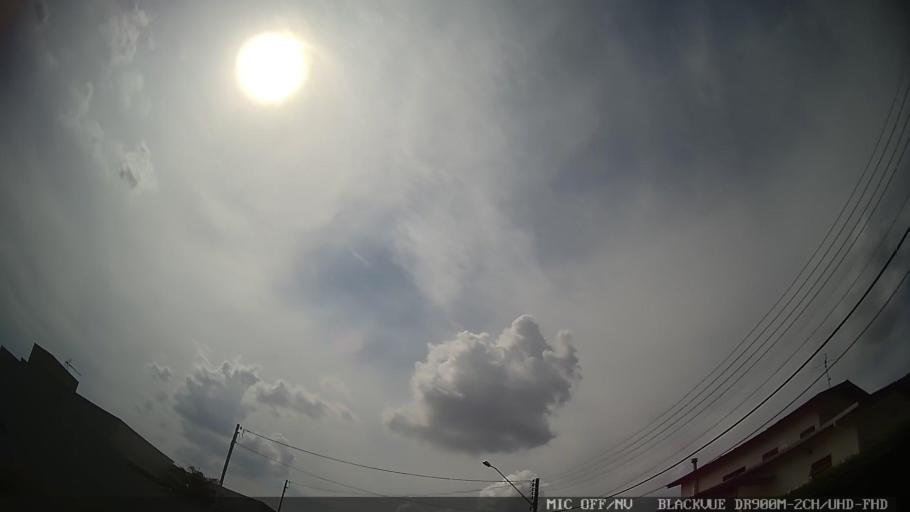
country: BR
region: Sao Paulo
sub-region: Braganca Paulista
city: Braganca Paulista
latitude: -22.9646
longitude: -46.5298
